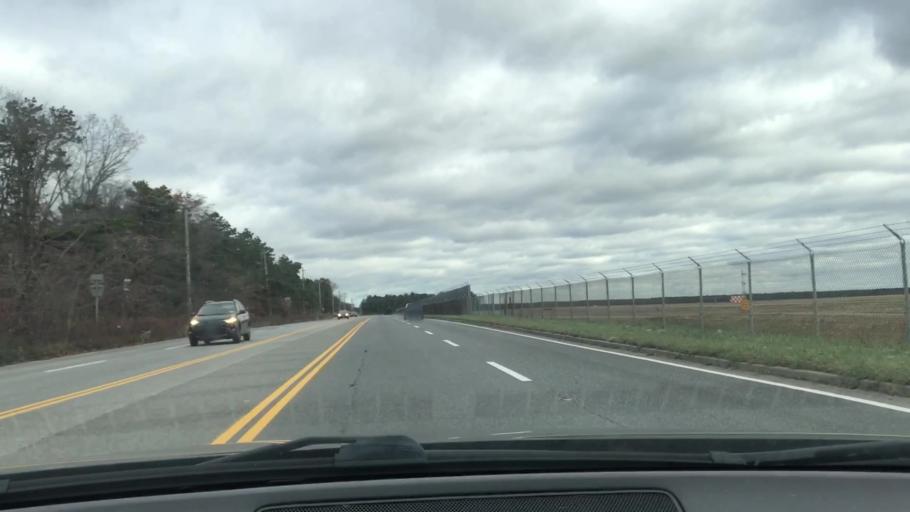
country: US
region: New York
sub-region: Suffolk County
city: Bohemia
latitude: 40.7896
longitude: -73.1150
